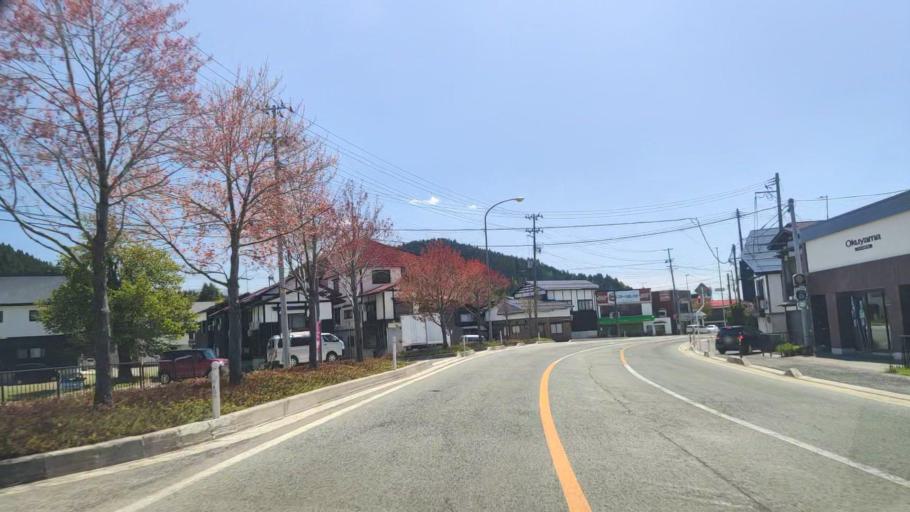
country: JP
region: Yamagata
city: Shinjo
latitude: 38.8832
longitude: 140.3368
